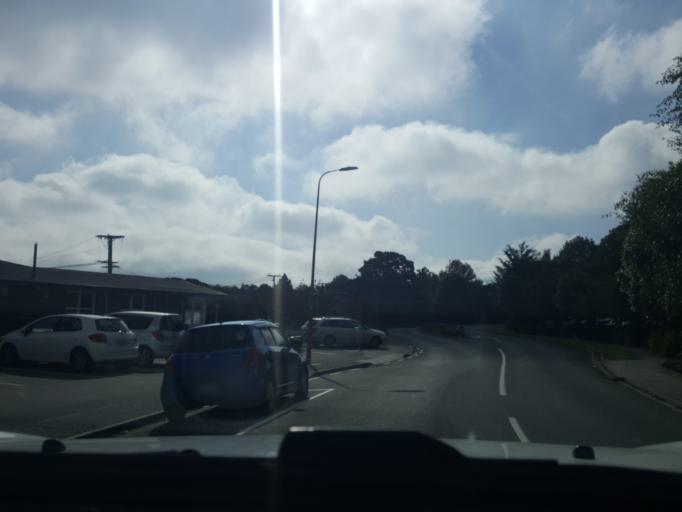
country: NZ
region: Waikato
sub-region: Hamilton City
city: Hamilton
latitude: -37.7500
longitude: 175.2776
